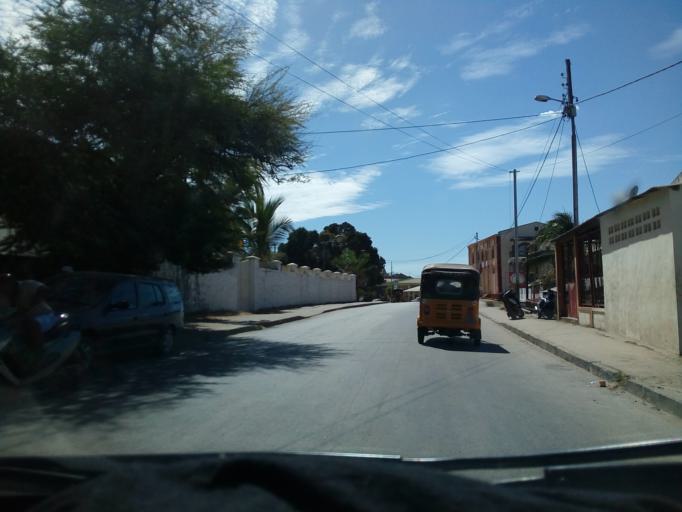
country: MG
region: Boeny
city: Mahajanga
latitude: -15.7134
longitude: 46.3171
